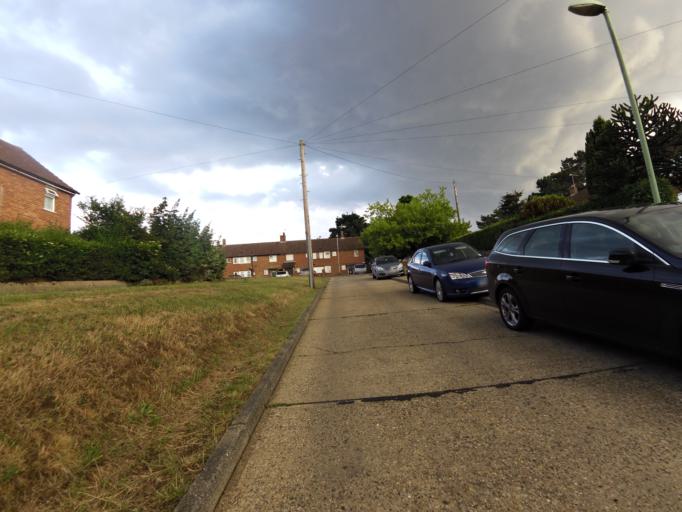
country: GB
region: England
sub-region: Suffolk
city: Ipswich
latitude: 52.0478
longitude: 1.1342
